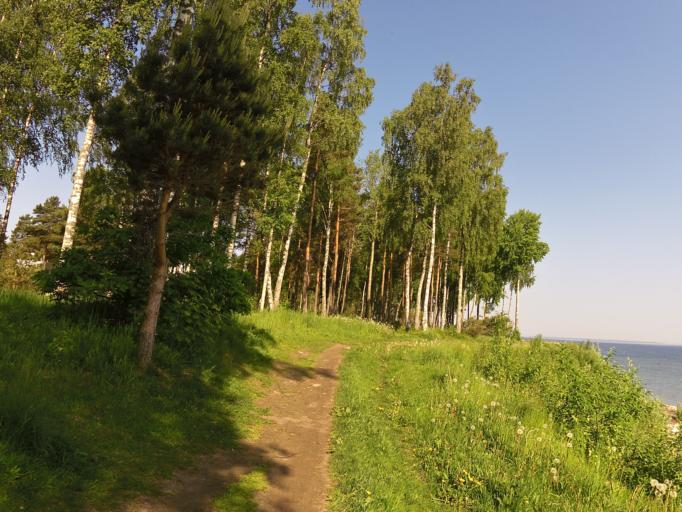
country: EE
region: Harju
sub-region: Harku vald
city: Tabasalu
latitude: 59.4433
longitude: 24.6224
